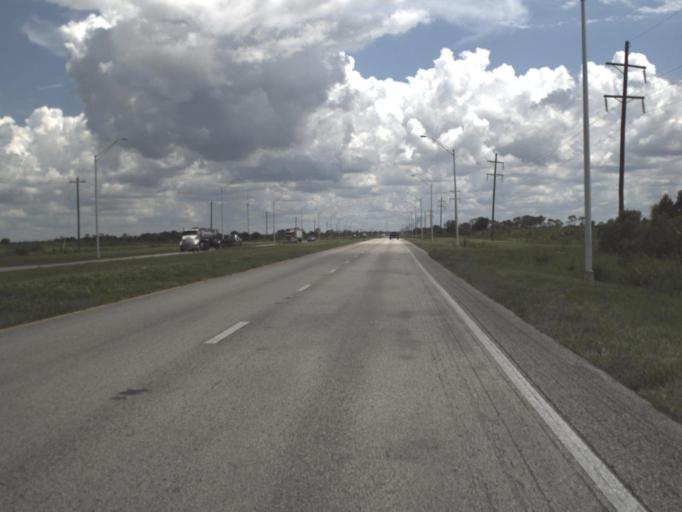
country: US
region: Florida
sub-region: Polk County
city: Babson Park
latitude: 27.8632
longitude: -81.3798
